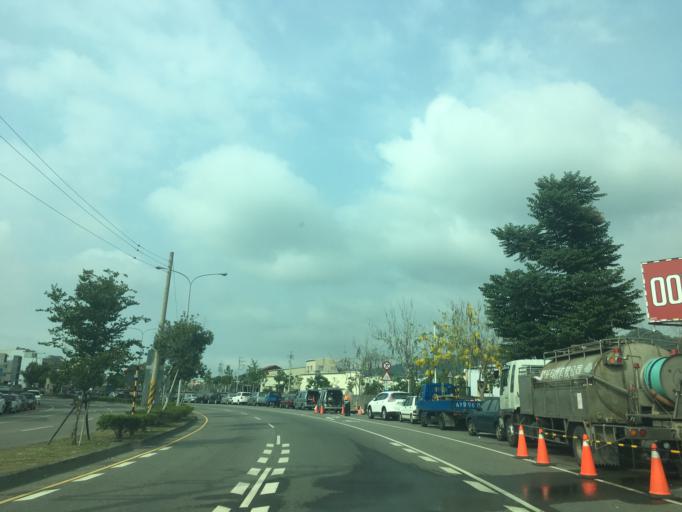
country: TW
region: Taiwan
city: Fengyuan
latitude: 24.2363
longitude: 120.7257
